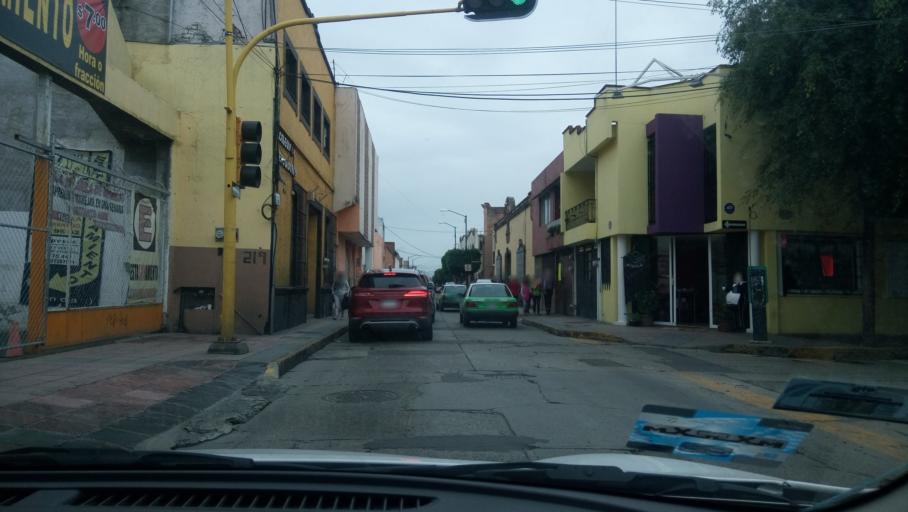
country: MX
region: Guanajuato
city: Leon
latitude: 21.1205
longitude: -101.6808
